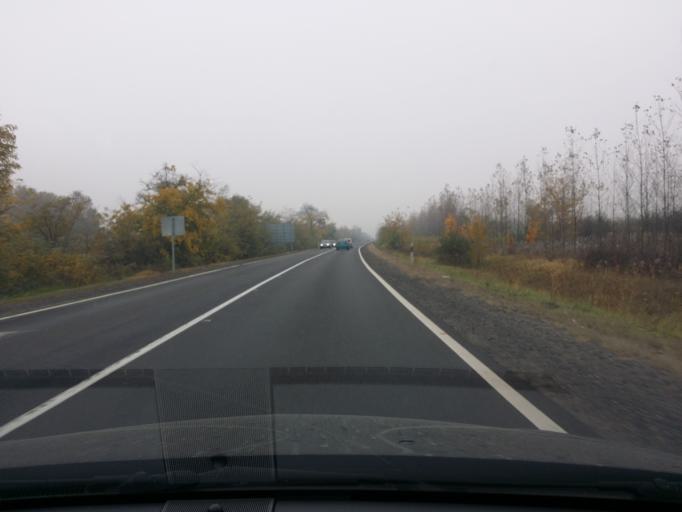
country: HU
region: Szabolcs-Szatmar-Bereg
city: Nyirbogdany
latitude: 48.0226
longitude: 21.8444
